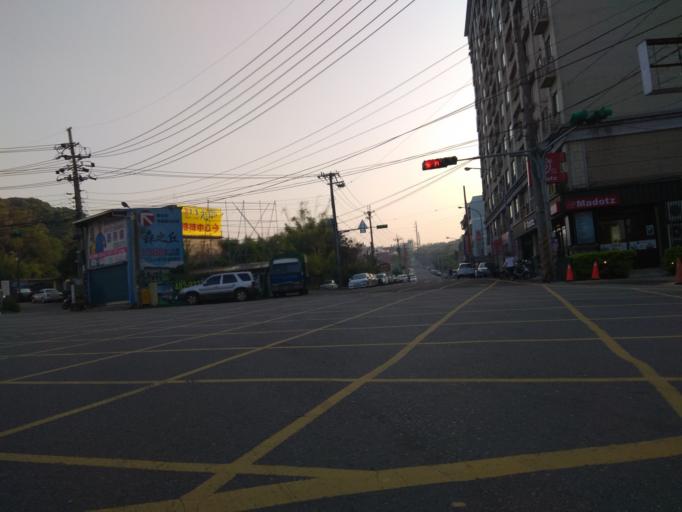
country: TW
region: Taiwan
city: Daxi
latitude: 24.9058
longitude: 121.1774
